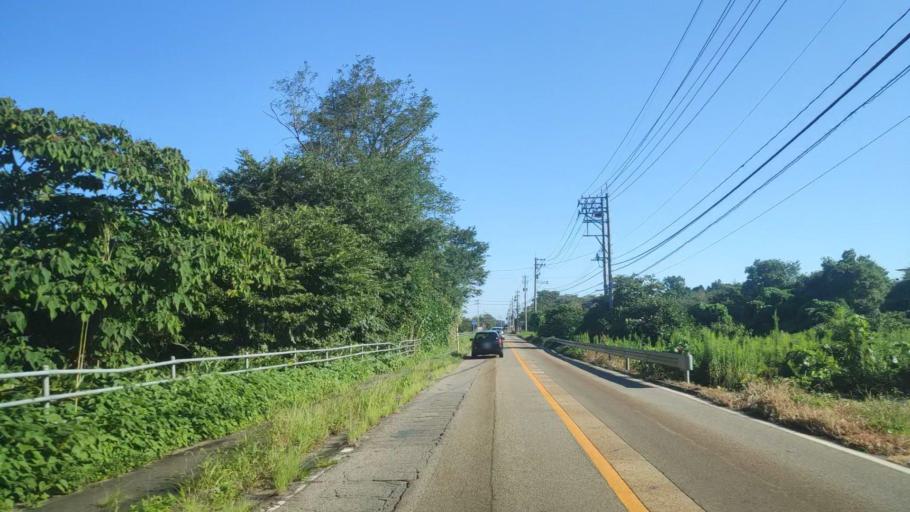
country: JP
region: Ishikawa
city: Hakui
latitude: 36.8461
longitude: 136.7674
